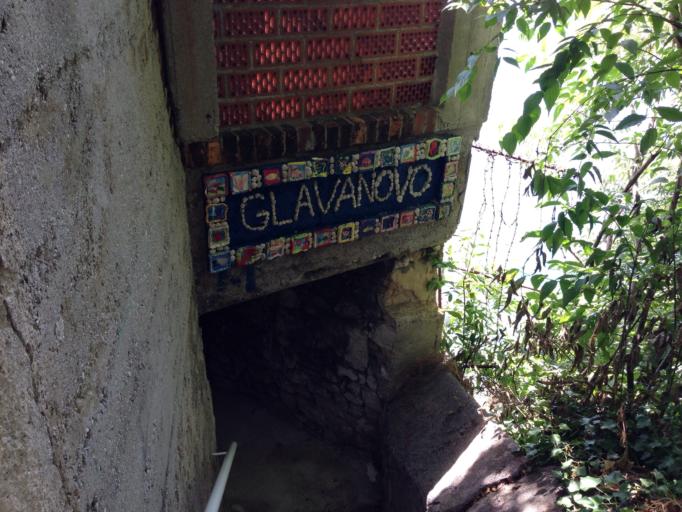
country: HR
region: Primorsko-Goranska
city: Cavle
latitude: 45.3158
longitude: 14.4695
